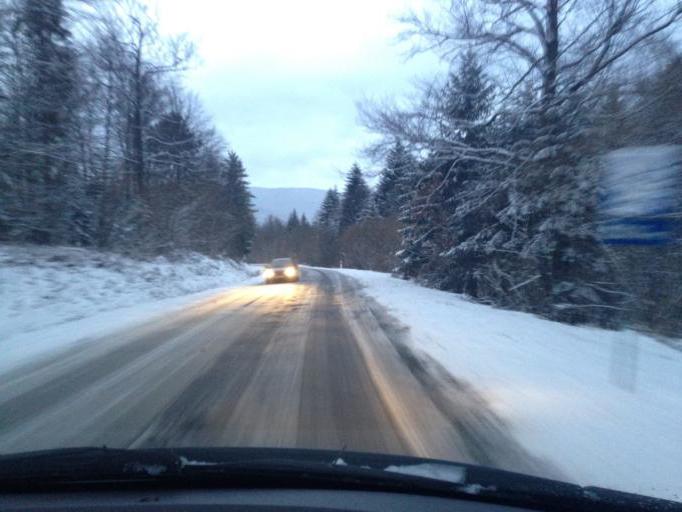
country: PL
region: Subcarpathian Voivodeship
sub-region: Powiat jasielski
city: Krempna
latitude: 49.5286
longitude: 21.5016
